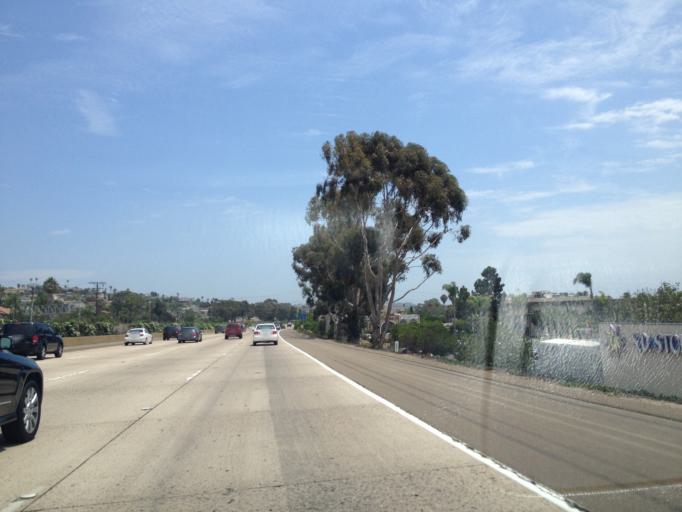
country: US
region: California
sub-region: San Diego County
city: La Jolla
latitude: 32.8055
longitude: -117.2150
